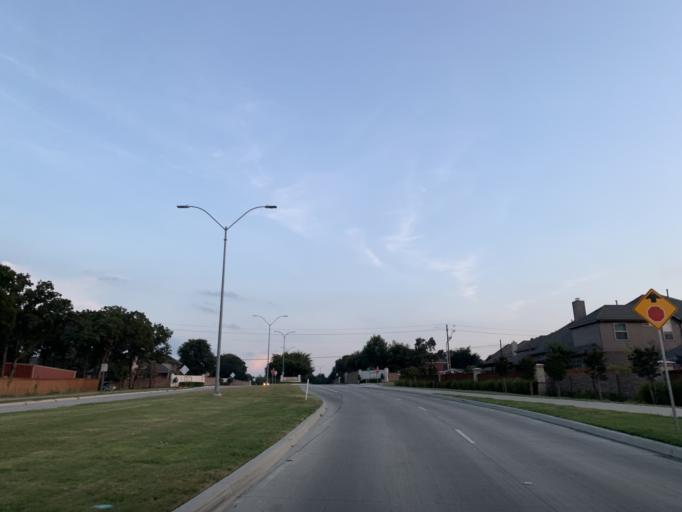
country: US
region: Texas
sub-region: Tarrant County
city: Keller
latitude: 32.9540
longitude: -97.2649
